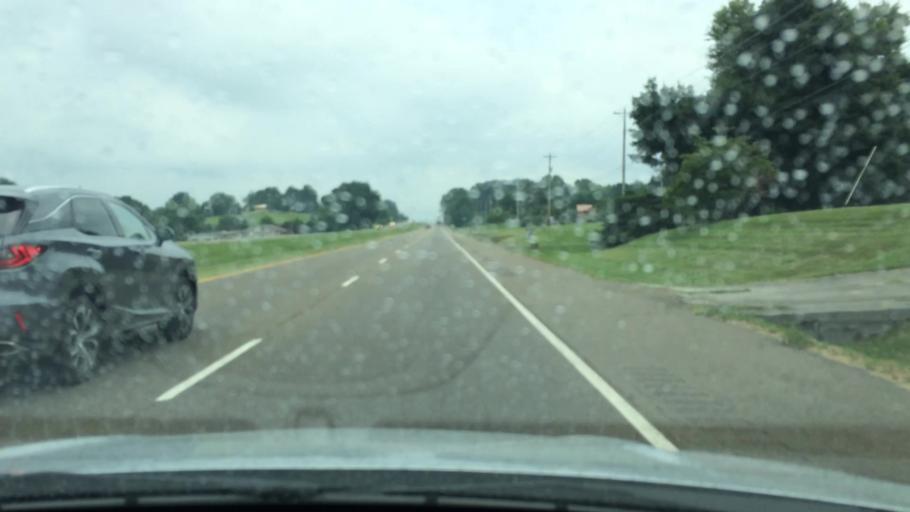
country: US
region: Tennessee
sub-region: Jefferson County
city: New Market
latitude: 36.1070
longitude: -83.5274
